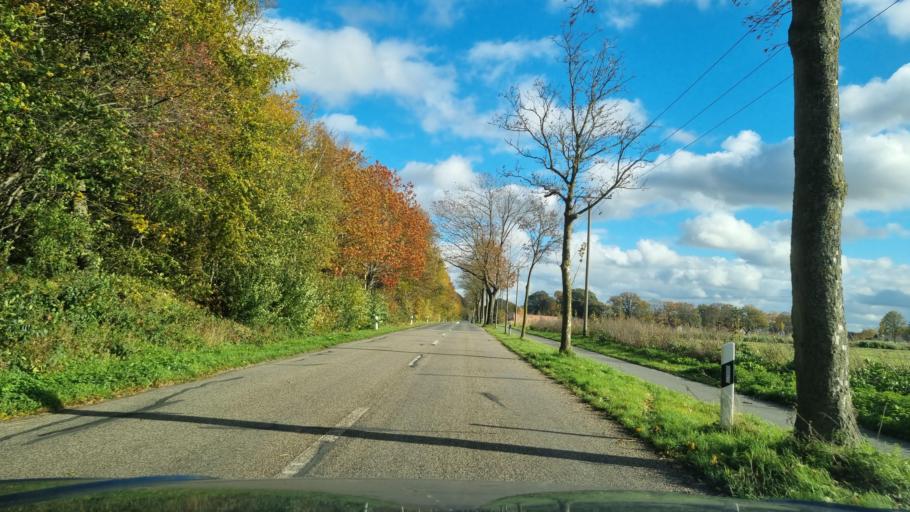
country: DE
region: North Rhine-Westphalia
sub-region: Regierungsbezirk Dusseldorf
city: Kleve
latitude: 51.7669
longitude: 6.1602
